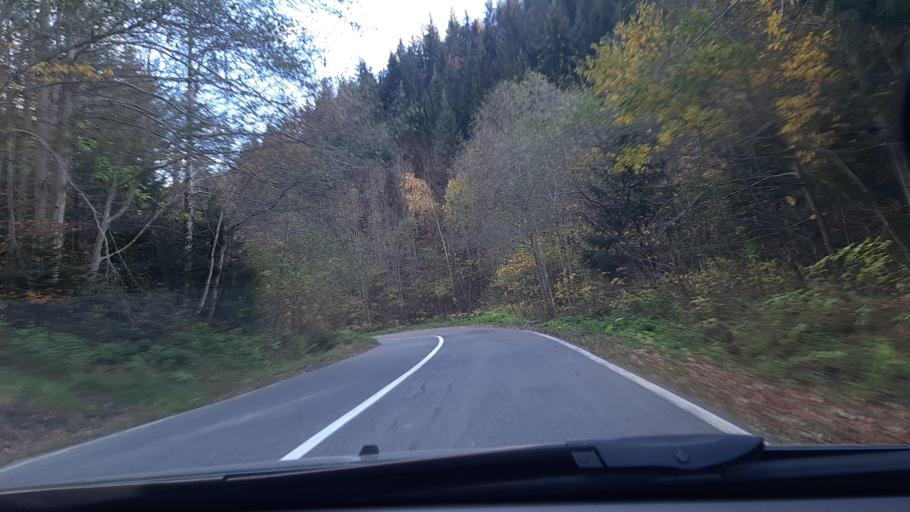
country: RO
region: Valcea
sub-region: Comuna Voineasa
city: Voineasa
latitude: 45.4372
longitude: 23.8617
